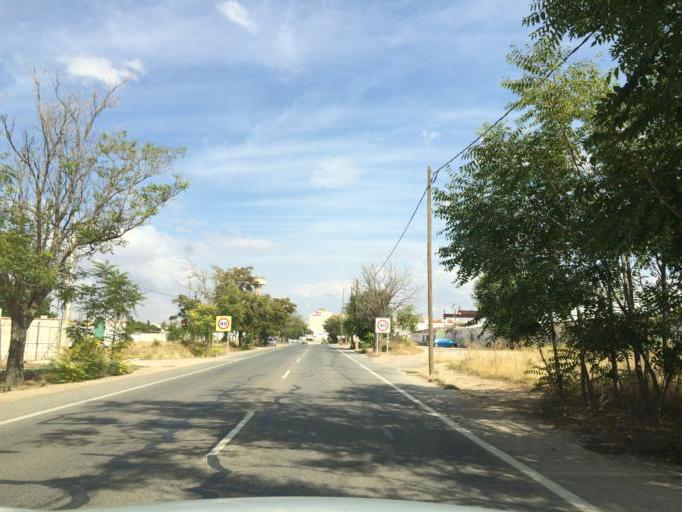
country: ES
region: Castille-La Mancha
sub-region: Provincia de Albacete
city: Albacete
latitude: 38.9976
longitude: -1.8824
